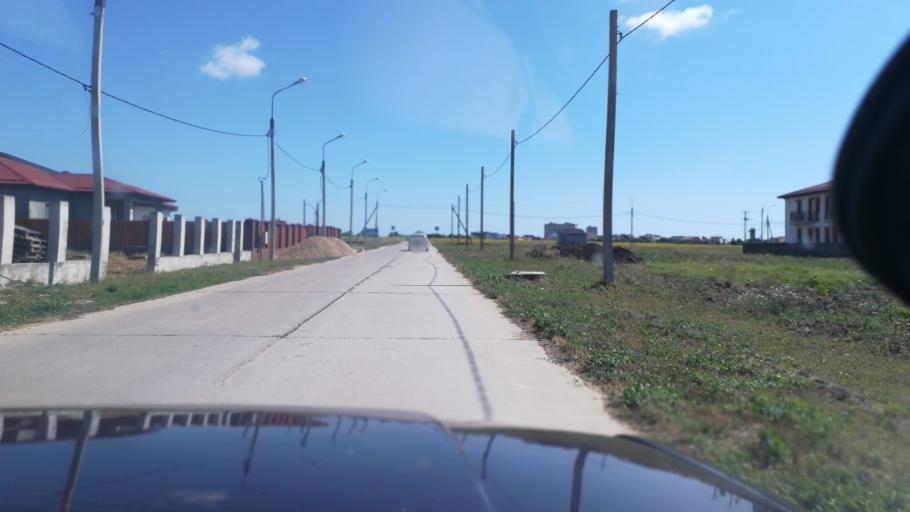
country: RU
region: Krasnodarskiy
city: Vityazevo
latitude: 44.9896
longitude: 37.2756
